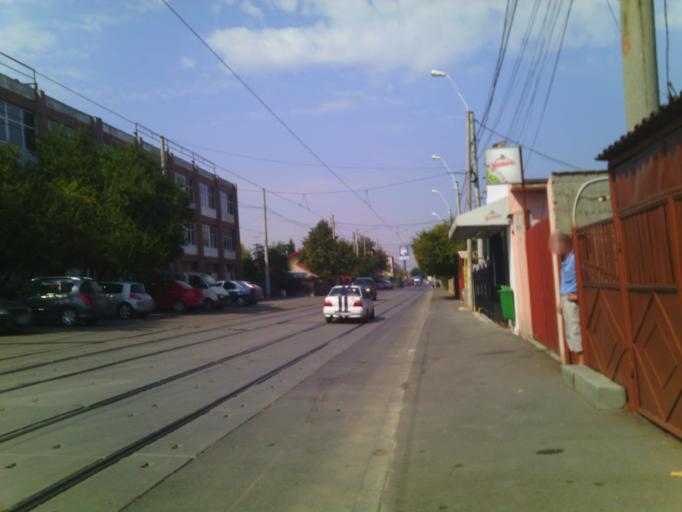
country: RO
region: Ilfov
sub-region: Comuna Jilava
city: Jilava
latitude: 44.3712
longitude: 26.0952
